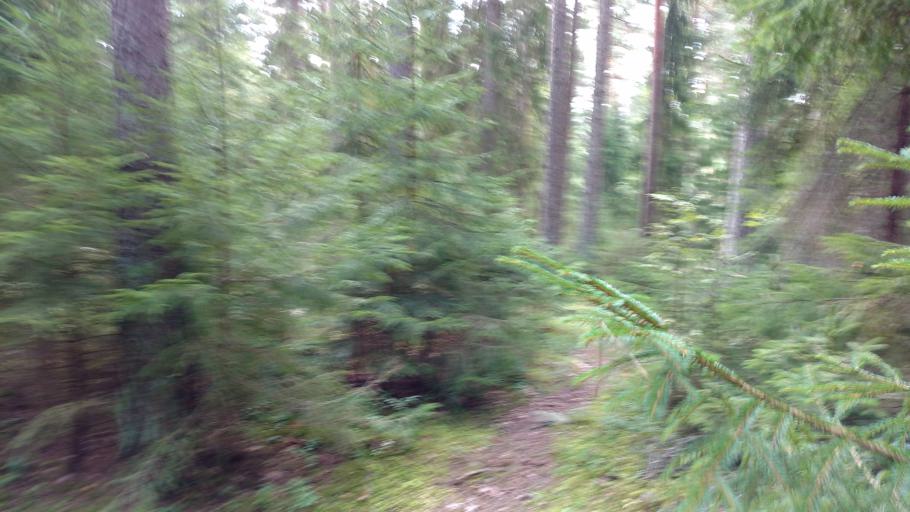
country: FI
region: Varsinais-Suomi
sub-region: Salo
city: Salo
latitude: 60.3649
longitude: 23.1854
